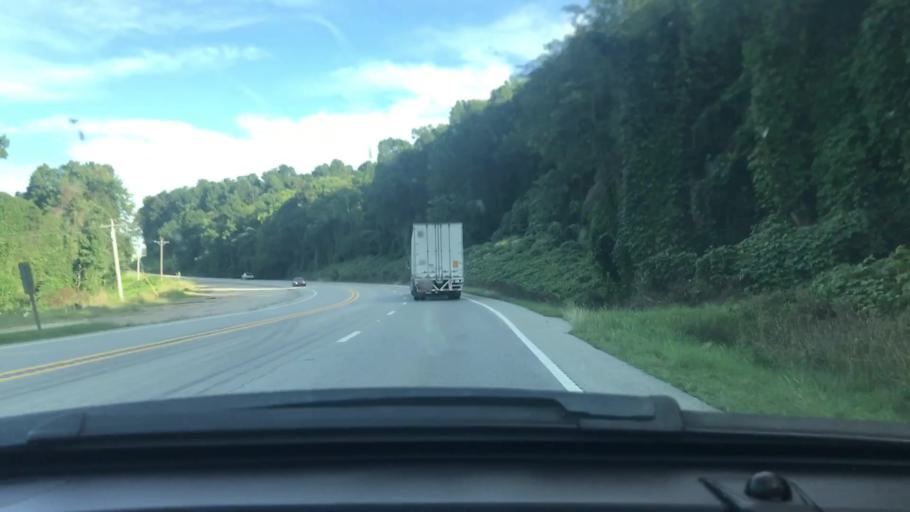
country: US
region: Arkansas
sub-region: Sharp County
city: Cherokee Village
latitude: 36.3016
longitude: -91.4116
